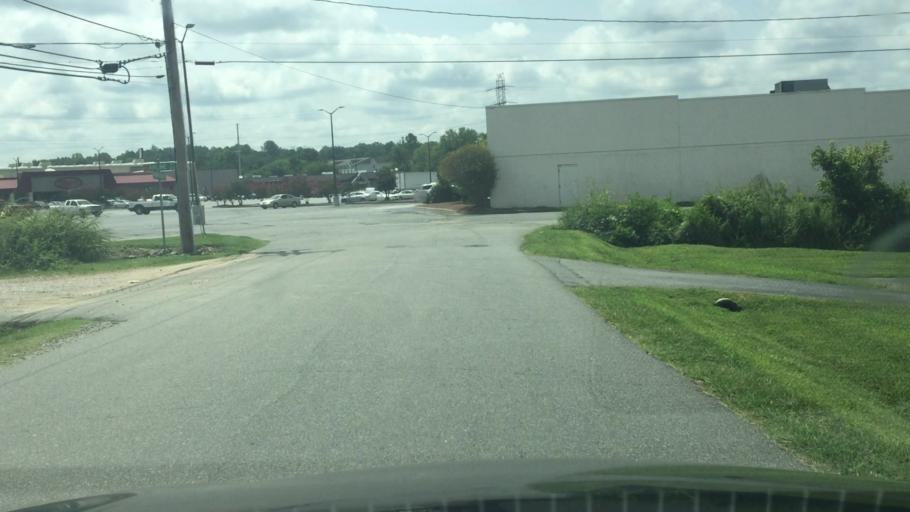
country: US
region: North Carolina
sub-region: Cabarrus County
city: Kannapolis
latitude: 35.4520
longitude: -80.6073
